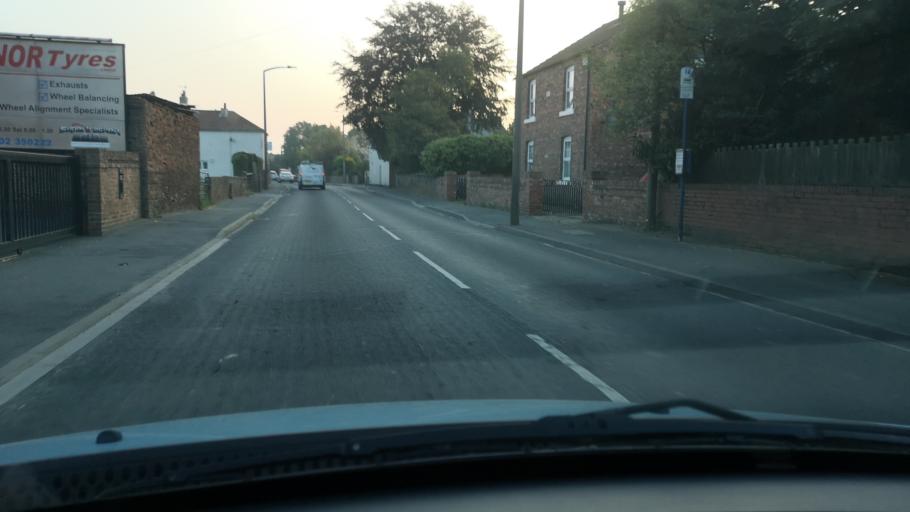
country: GB
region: England
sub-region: Doncaster
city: Stainforth
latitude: 53.5987
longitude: -1.0361
